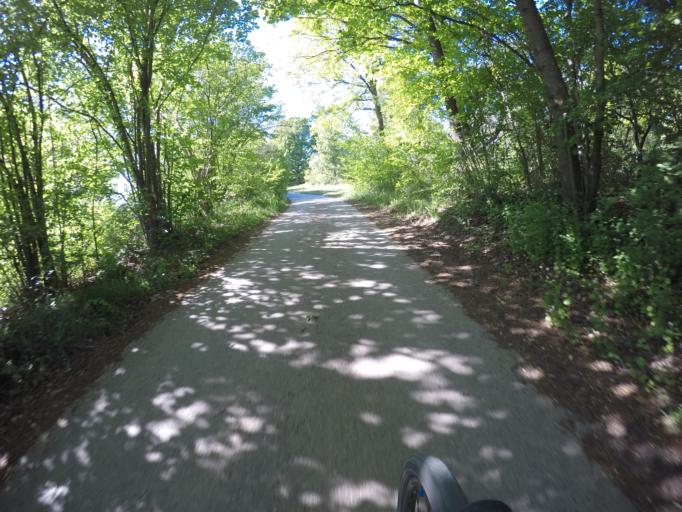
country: DE
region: Baden-Wuerttemberg
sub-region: Karlsruhe Region
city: Friolzheim
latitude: 48.8250
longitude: 8.8482
